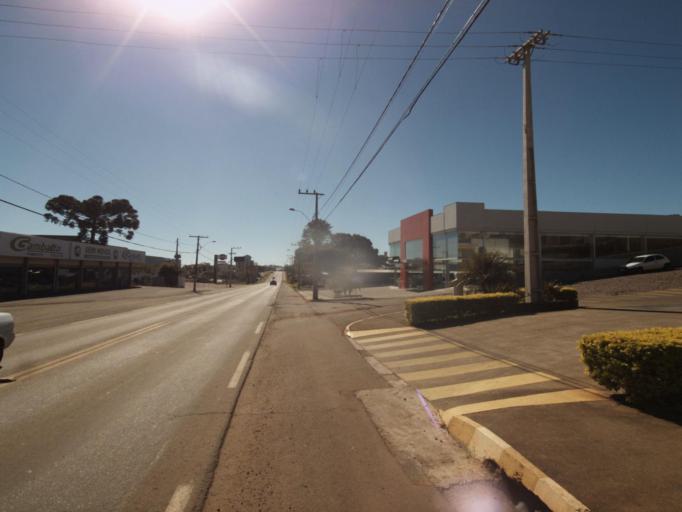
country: AR
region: Misiones
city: Bernardo de Irigoyen
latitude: -26.7453
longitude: -53.5186
